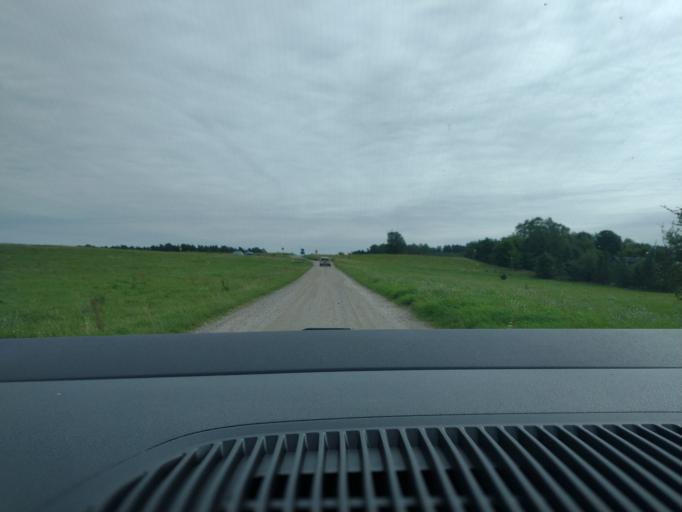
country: SE
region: Skane
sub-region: Lunds Kommun
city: Veberod
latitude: 55.6880
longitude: 13.4988
